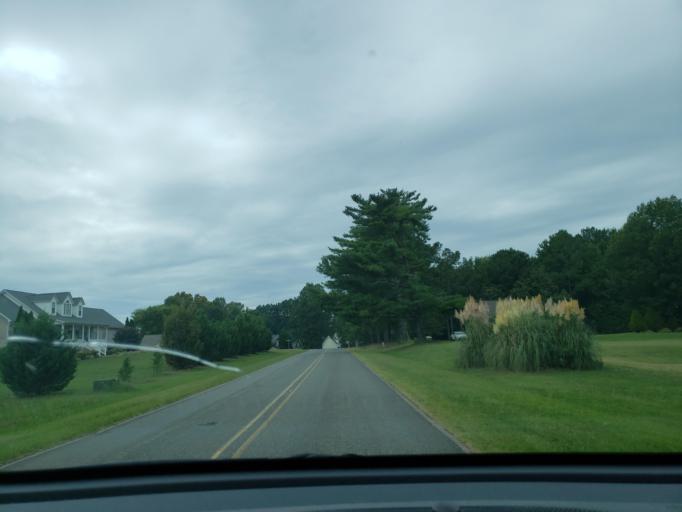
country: US
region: North Carolina
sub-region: Vance County
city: Henderson
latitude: 36.4012
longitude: -78.3720
